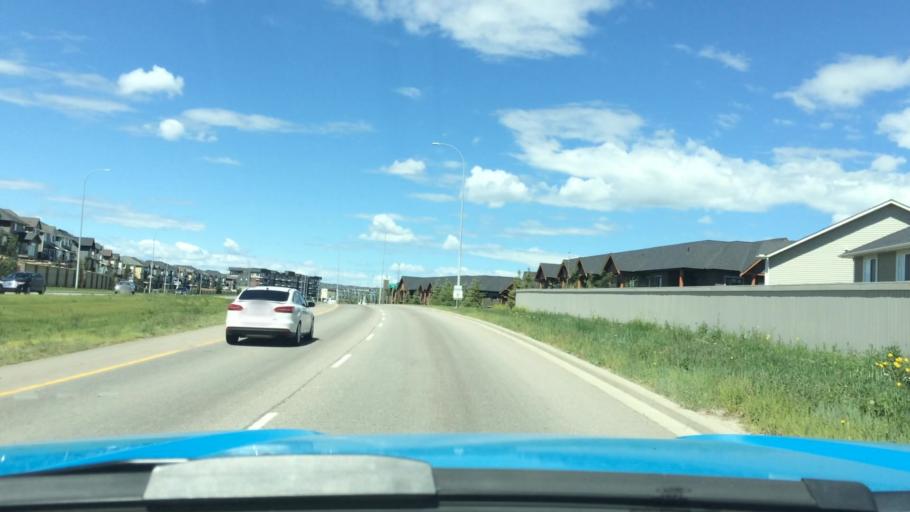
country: CA
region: Alberta
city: Calgary
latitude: 51.1644
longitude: -114.1450
